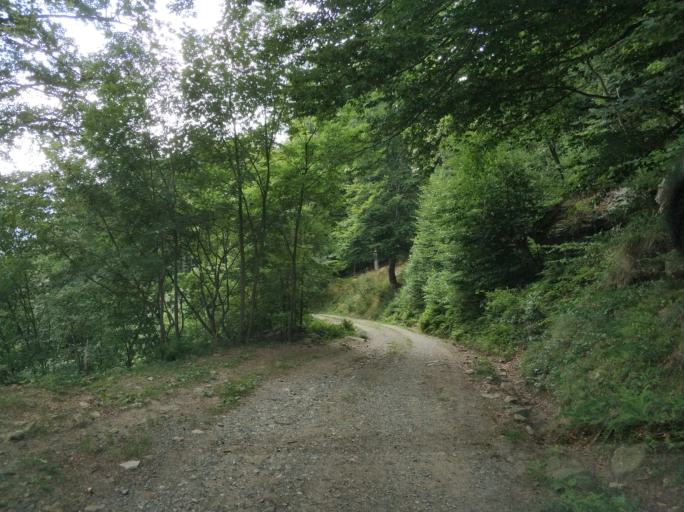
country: IT
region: Piedmont
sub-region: Provincia di Torino
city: Viu
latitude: 45.1970
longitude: 7.3673
